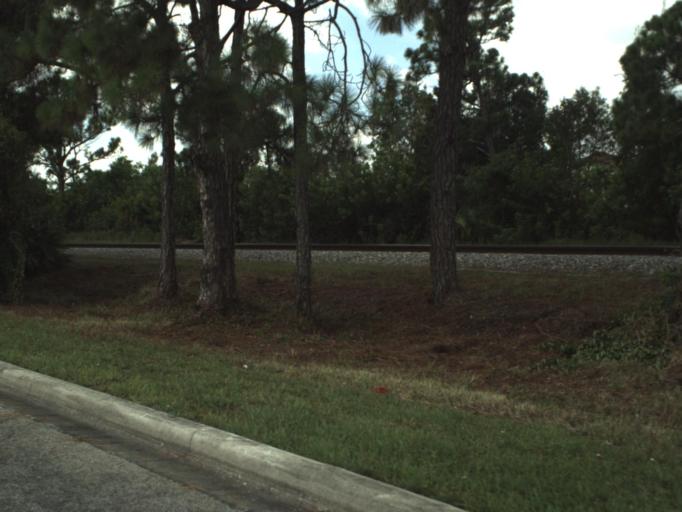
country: US
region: Florida
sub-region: Palm Beach County
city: North Palm Beach
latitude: 26.8416
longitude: -80.0947
